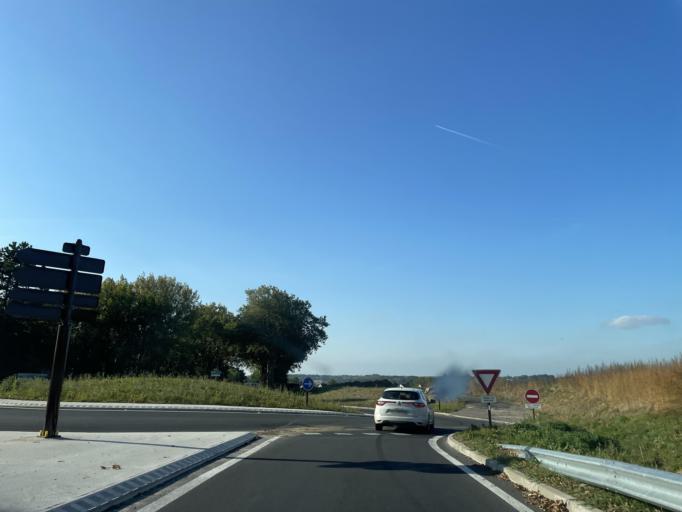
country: FR
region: Ile-de-France
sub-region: Departement de Seine-et-Marne
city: La Chapelle-sur-Crecy
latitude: 48.8479
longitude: 2.9409
